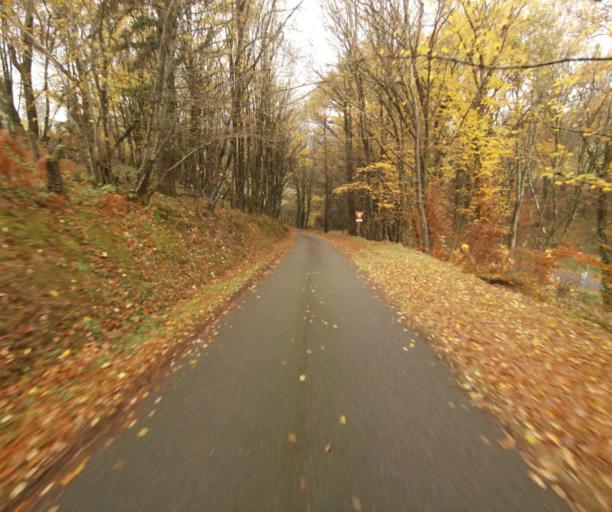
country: FR
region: Limousin
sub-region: Departement de la Correze
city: Cosnac
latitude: 45.1828
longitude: 1.6295
